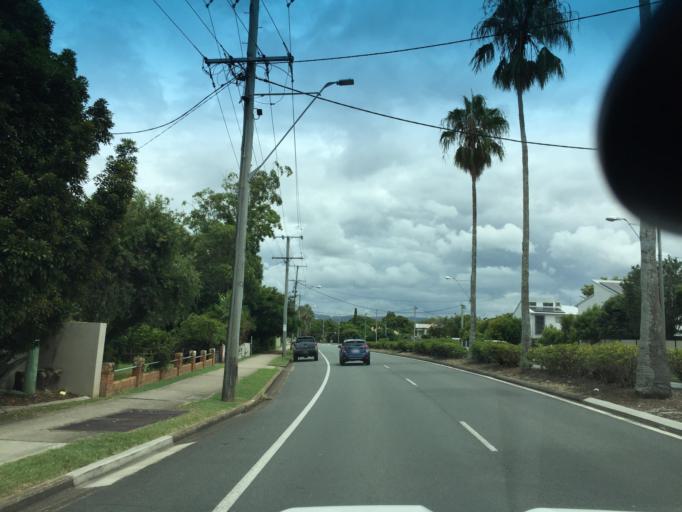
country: AU
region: Queensland
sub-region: Moreton Bay
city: Caboolture
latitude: -27.0846
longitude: 152.9464
